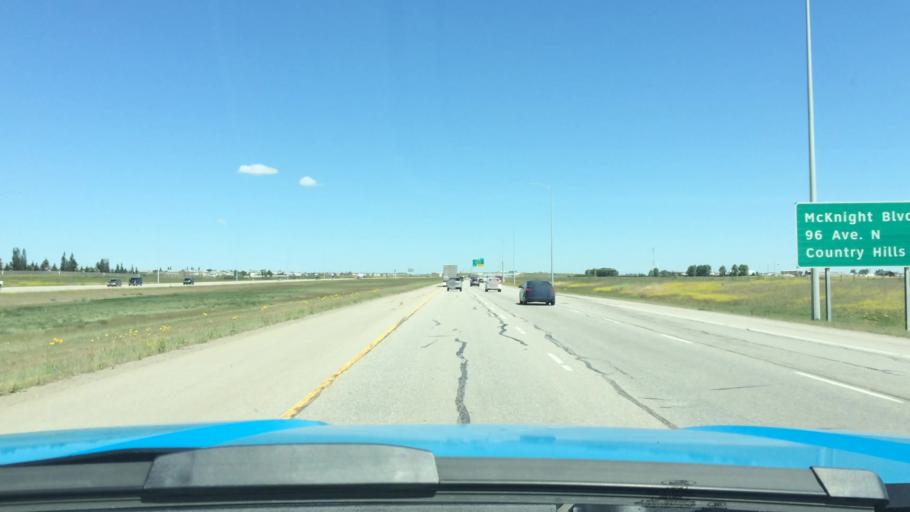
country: CA
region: Alberta
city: Chestermere
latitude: 51.0760
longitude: -113.9203
